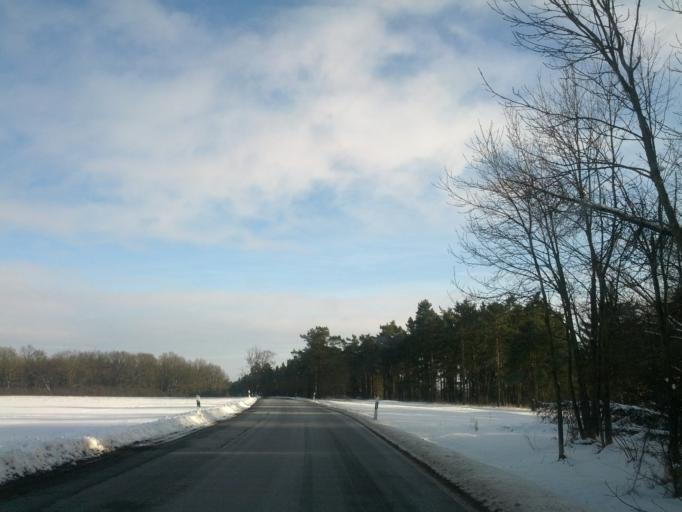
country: DE
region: Thuringia
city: Weberstedt
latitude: 51.0526
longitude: 10.4964
